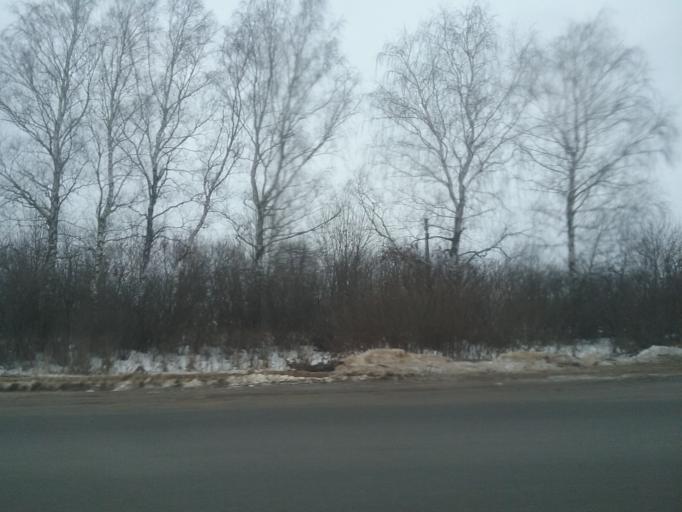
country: RU
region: Tula
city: Bolokhovo
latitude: 54.0684
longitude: 37.7963
